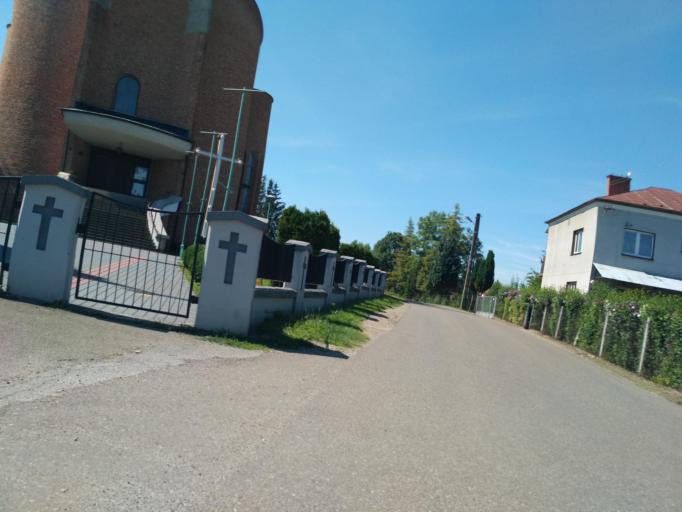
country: PL
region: Subcarpathian Voivodeship
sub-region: Powiat sanocki
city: Dlugie
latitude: 49.5765
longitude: 22.0410
